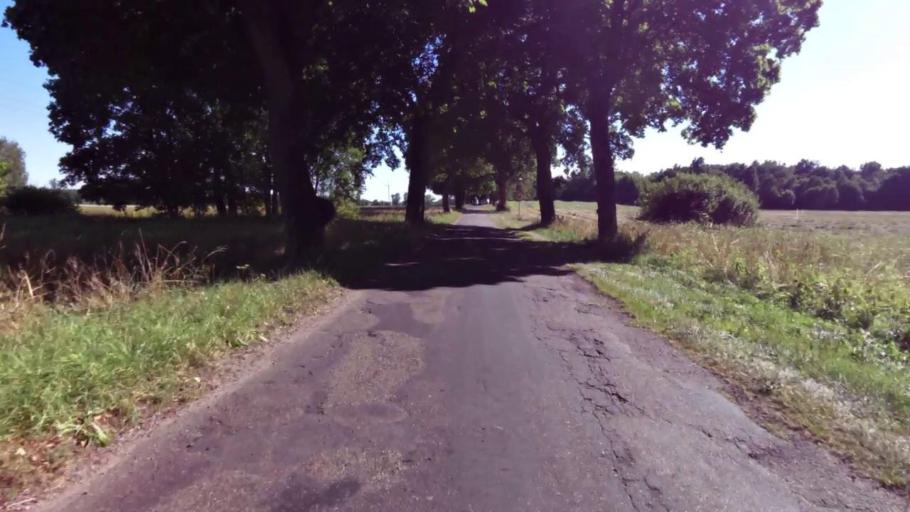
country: PL
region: West Pomeranian Voivodeship
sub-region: Powiat szczecinecki
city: Szczecinek
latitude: 53.7781
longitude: 16.6770
